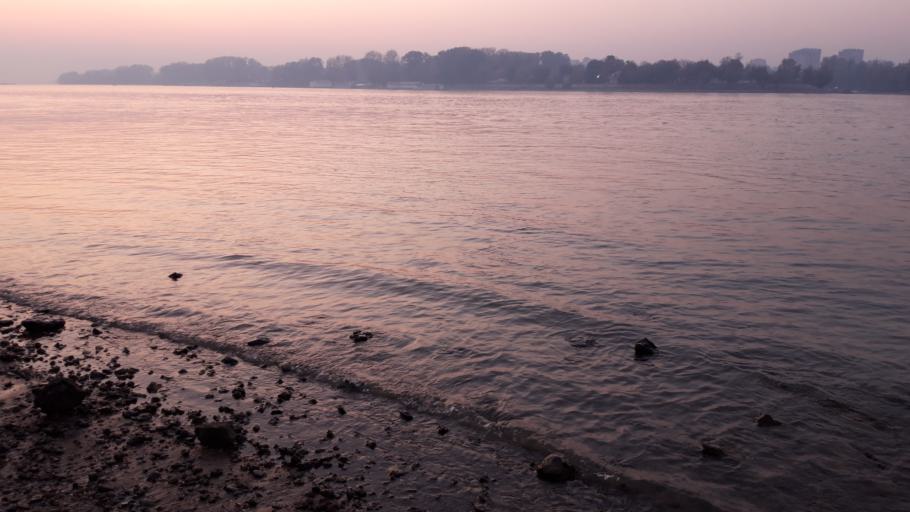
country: RS
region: Autonomna Pokrajina Vojvodina
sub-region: Juznobacki Okrug
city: Novi Sad
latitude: 45.2310
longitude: 19.8496
